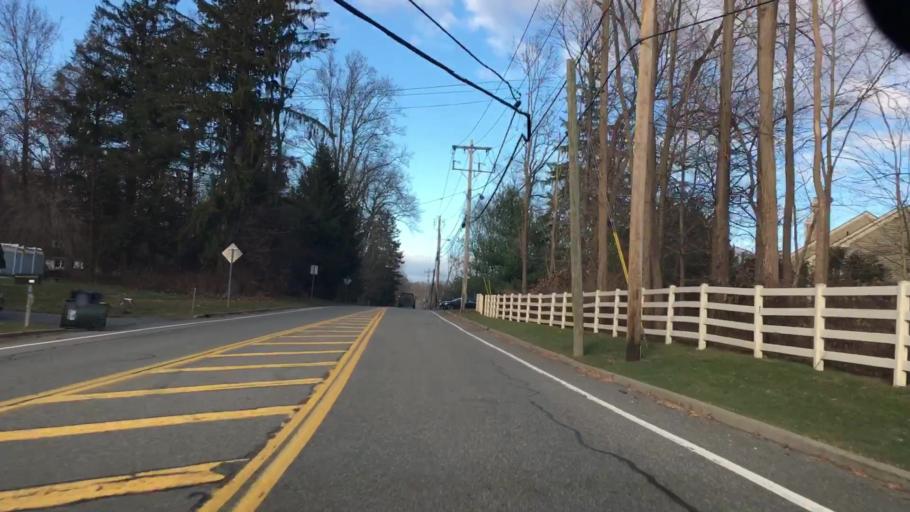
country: US
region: New York
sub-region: Putnam County
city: Carmel
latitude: 41.4350
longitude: -73.6533
